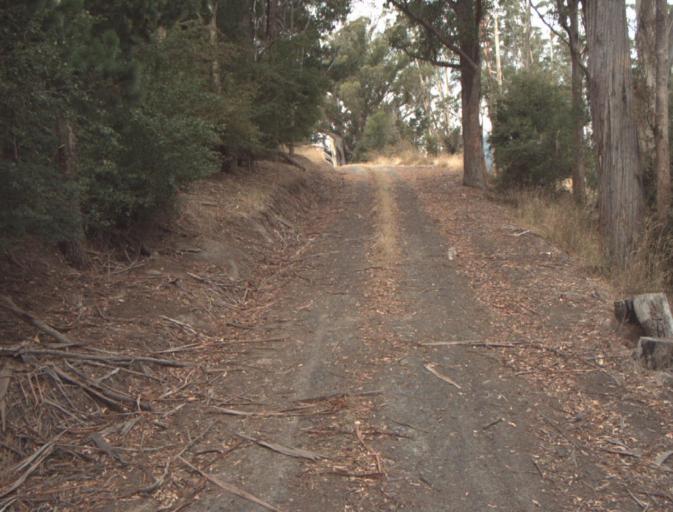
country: AU
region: Tasmania
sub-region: Launceston
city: Mayfield
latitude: -41.2488
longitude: 147.1977
